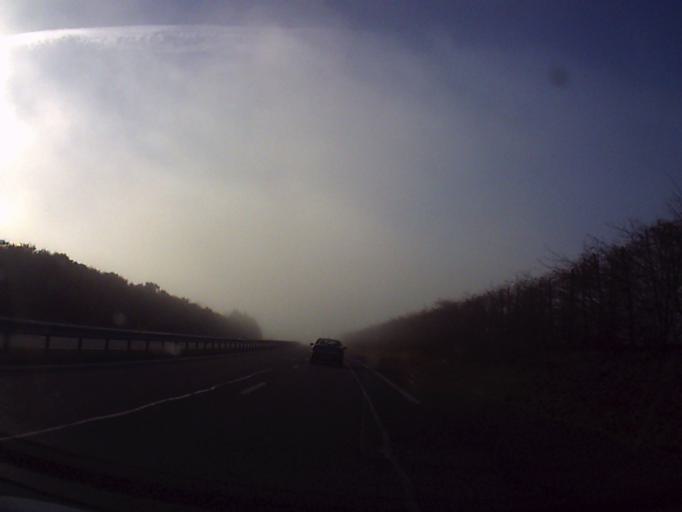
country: FR
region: Brittany
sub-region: Departement d'Ille-et-Vilaine
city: Plelan-le-Grand
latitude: 47.9739
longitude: -2.0977
